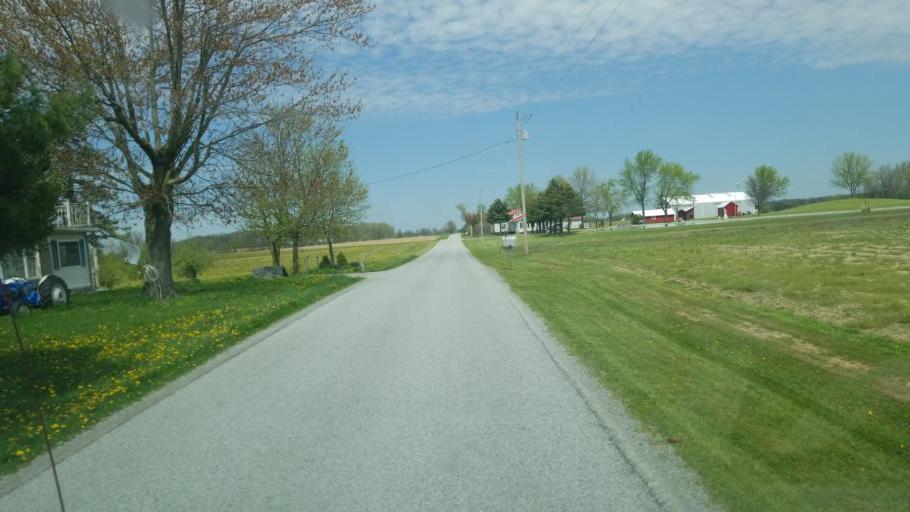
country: US
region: Ohio
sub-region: Hardin County
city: Ada
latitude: 40.8025
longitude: -83.8990
